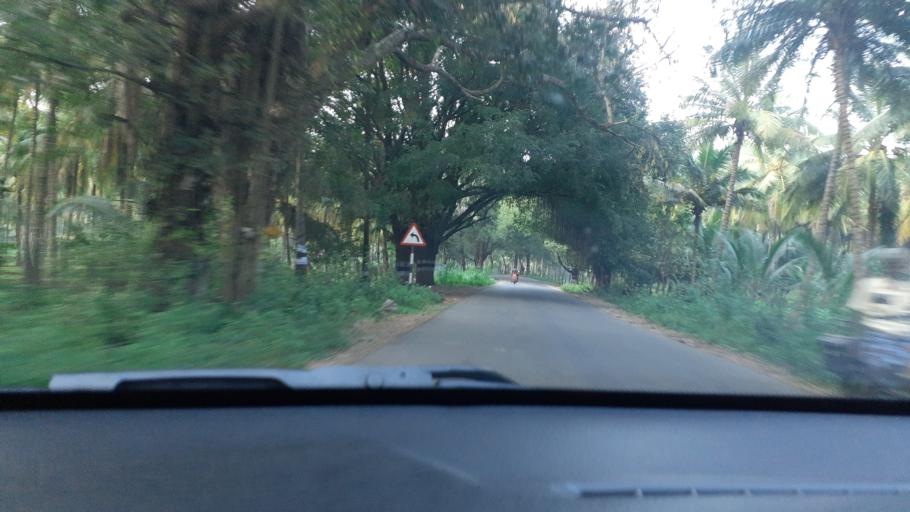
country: IN
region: Tamil Nadu
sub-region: Dindigul
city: Ayakudi
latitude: 10.4127
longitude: 77.5381
